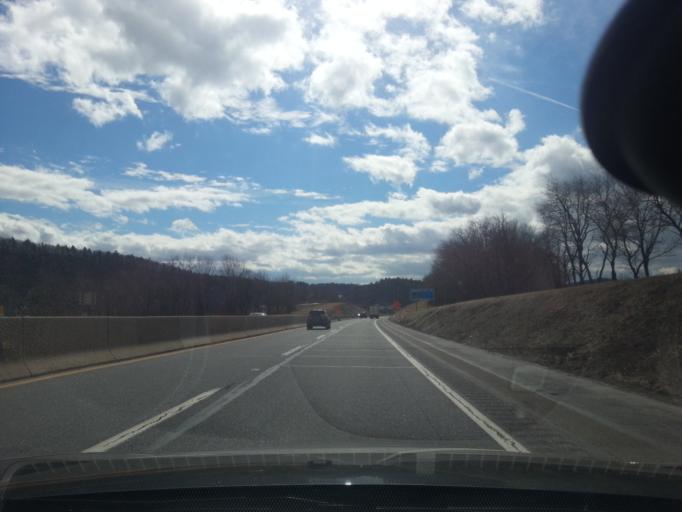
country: US
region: Pennsylvania
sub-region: Carbon County
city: Weissport East
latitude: 40.8471
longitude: -75.6587
